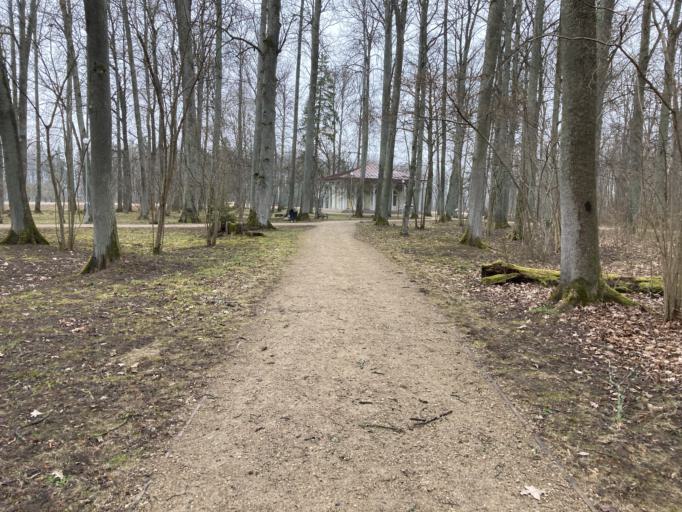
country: LT
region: Siauliu apskritis
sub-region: Joniskis
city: Joniskis
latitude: 56.4257
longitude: 23.7013
